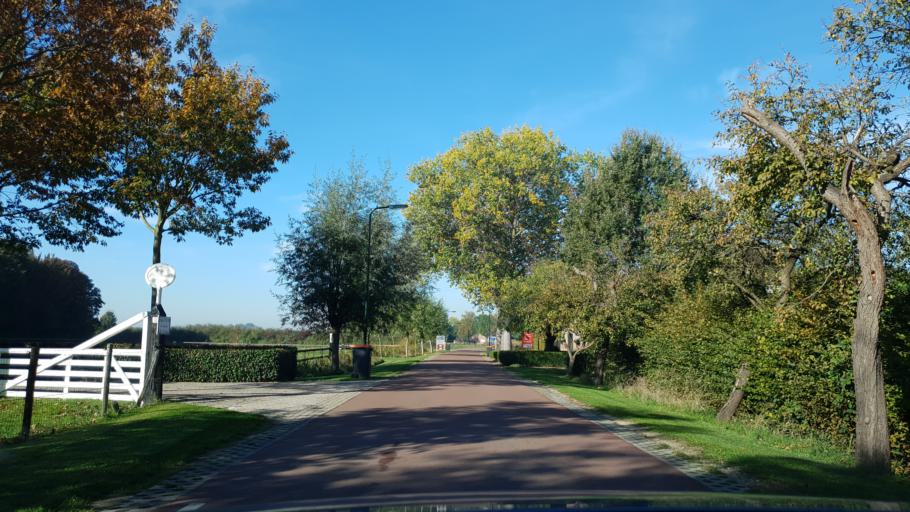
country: NL
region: Gelderland
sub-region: Gemeente Beuningen
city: Beuningen
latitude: 51.8598
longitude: 5.7495
